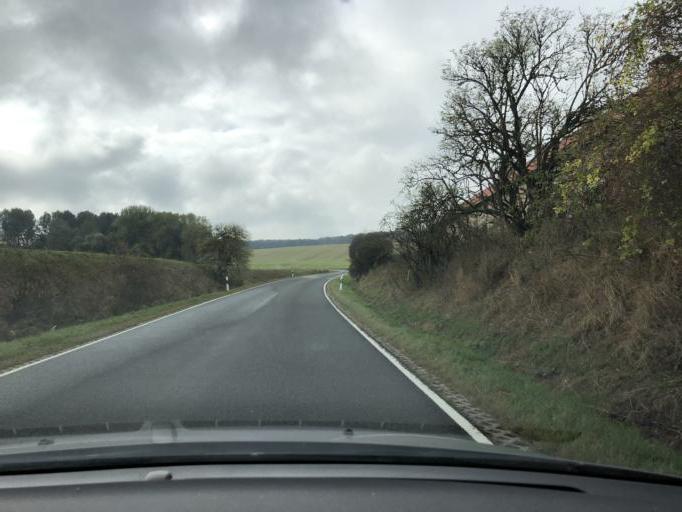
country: DE
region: Thuringia
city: Heuthen
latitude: 51.3262
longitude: 10.2206
